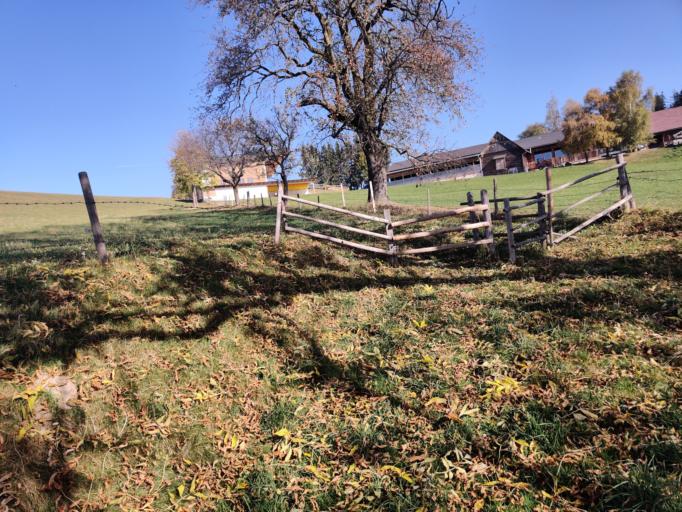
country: AT
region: Styria
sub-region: Politischer Bezirk Hartberg-Fuerstenfeld
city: Sankt Jakob im Walde
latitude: 47.4756
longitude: 15.7966
